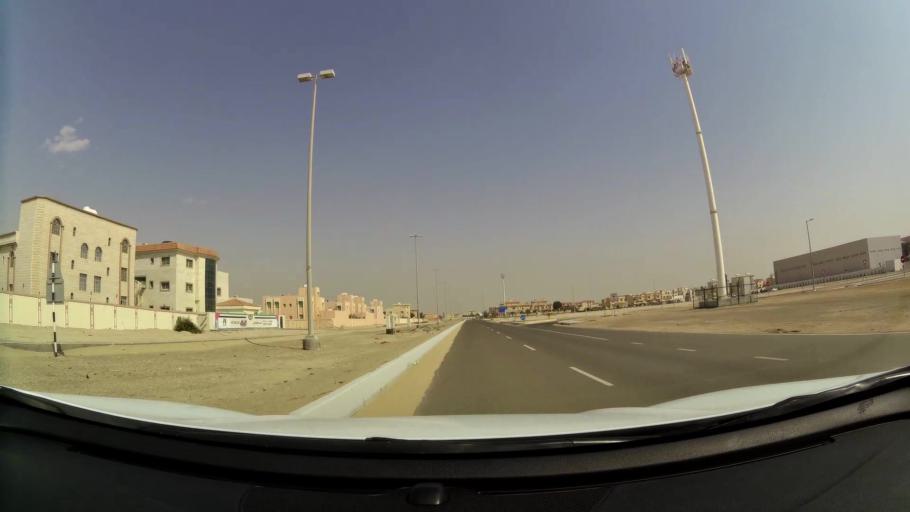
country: AE
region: Abu Dhabi
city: Abu Dhabi
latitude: 24.3413
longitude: 54.5558
